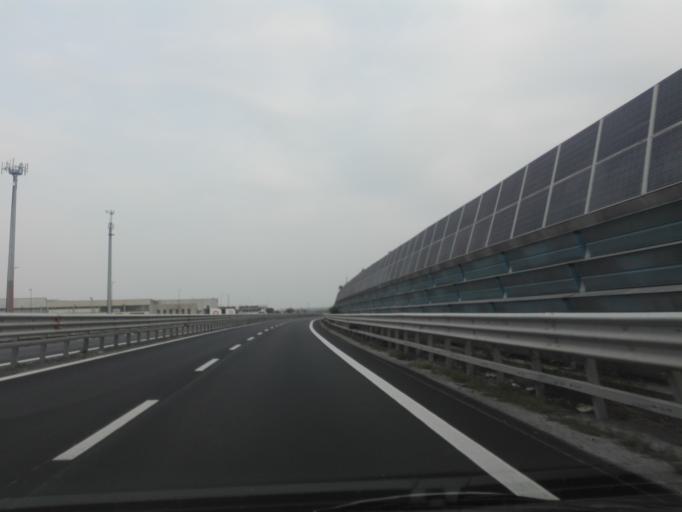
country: IT
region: Veneto
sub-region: Provincia di Verona
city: Vallese
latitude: 45.3295
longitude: 11.0800
